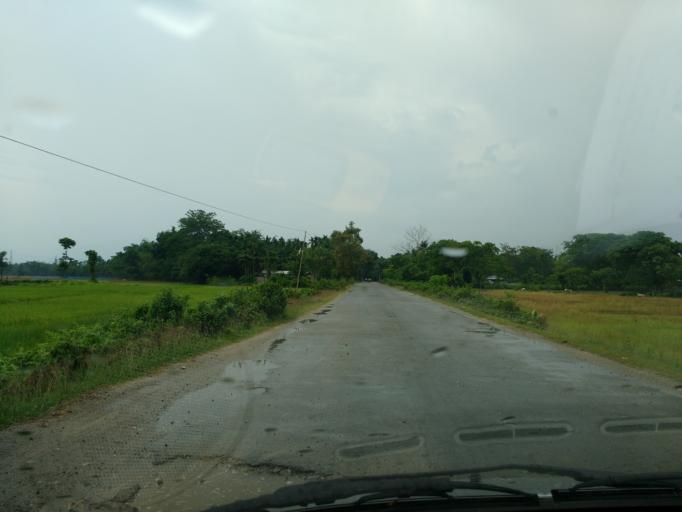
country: IN
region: Assam
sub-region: Udalguri
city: Udalguri
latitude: 26.7263
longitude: 92.2115
